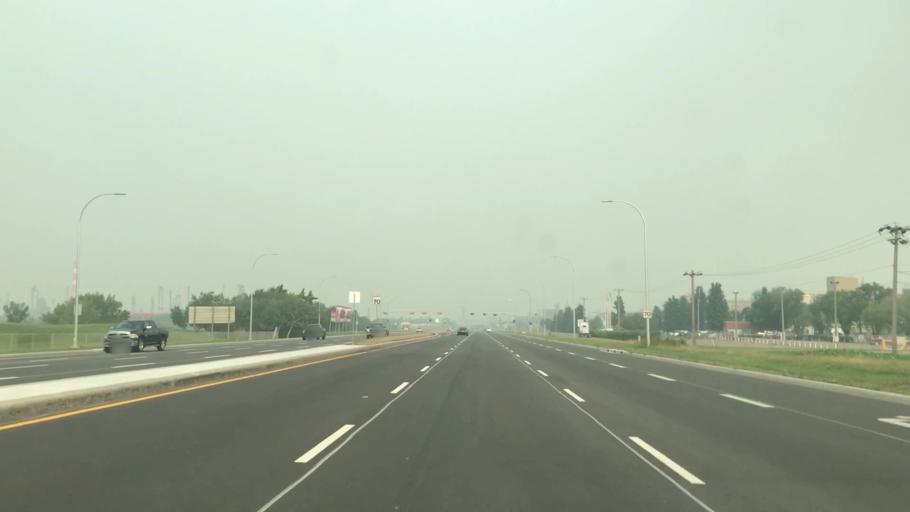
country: CA
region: Alberta
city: Edmonton
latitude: 53.5423
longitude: -113.4146
